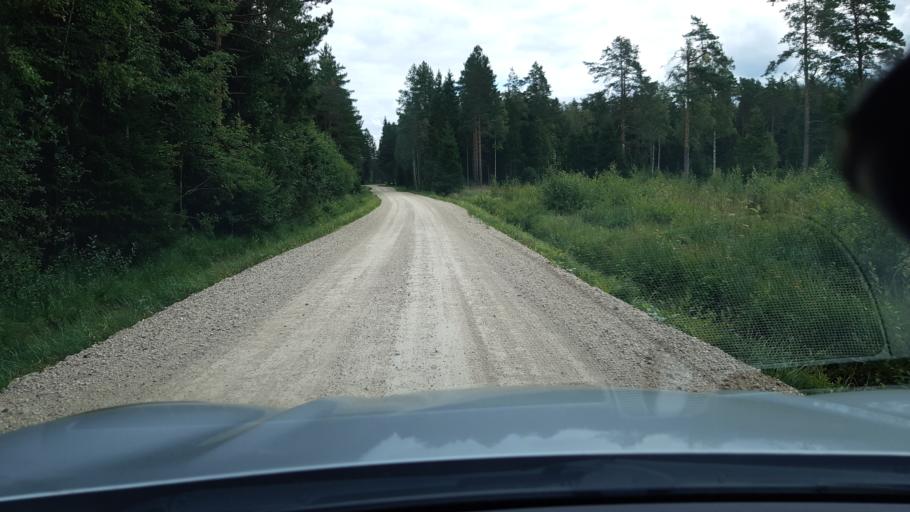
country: EE
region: Raplamaa
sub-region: Jaervakandi vald
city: Jarvakandi
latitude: 58.8049
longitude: 24.8217
